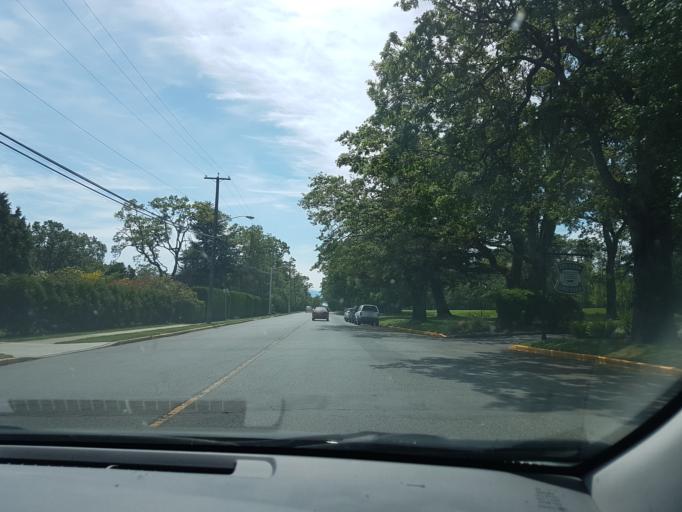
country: CA
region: British Columbia
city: Oak Bay
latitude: 48.4498
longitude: -123.3086
